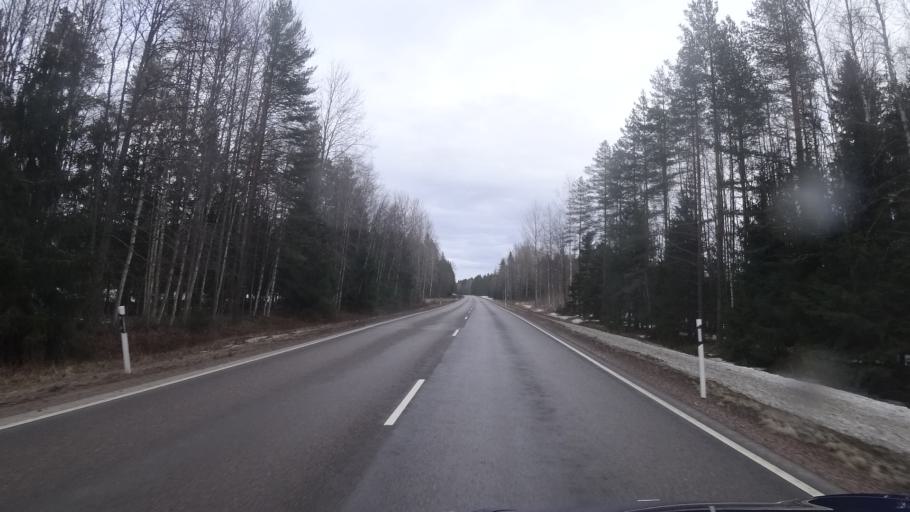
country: FI
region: Kymenlaakso
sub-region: Kouvola
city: Elimaeki
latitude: 60.6903
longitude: 26.6177
